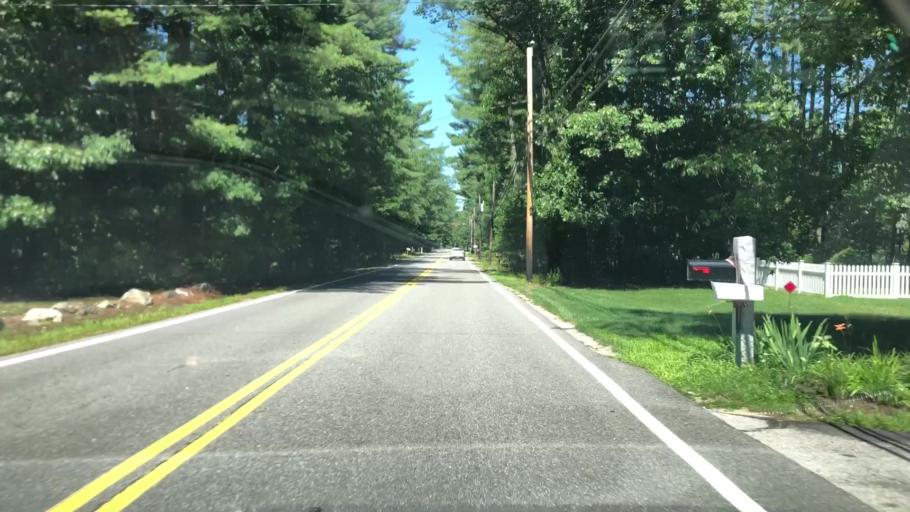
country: US
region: New Hampshire
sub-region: Hillsborough County
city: Milford
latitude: 42.8362
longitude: -71.5958
